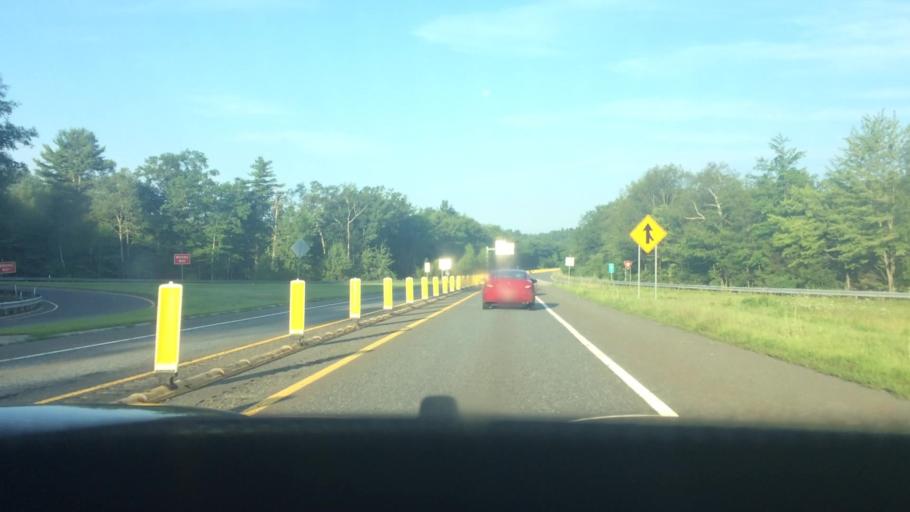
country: US
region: Massachusetts
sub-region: Worcester County
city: Athol
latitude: 42.5701
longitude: -72.2029
